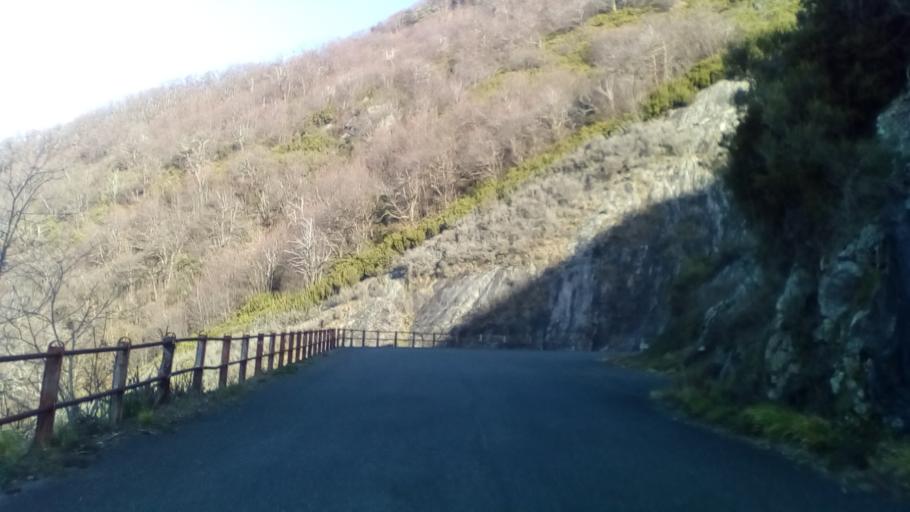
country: IT
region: Tuscany
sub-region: Provincia di Massa-Carrara
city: Montignoso
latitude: 44.0597
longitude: 10.1856
